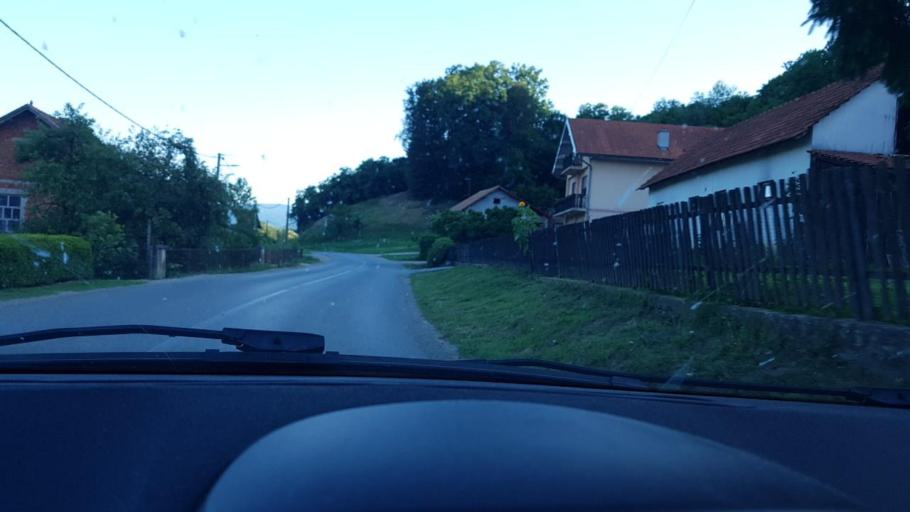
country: HR
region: Krapinsko-Zagorska
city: Bedekovcina
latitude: 46.0609
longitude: 16.0038
